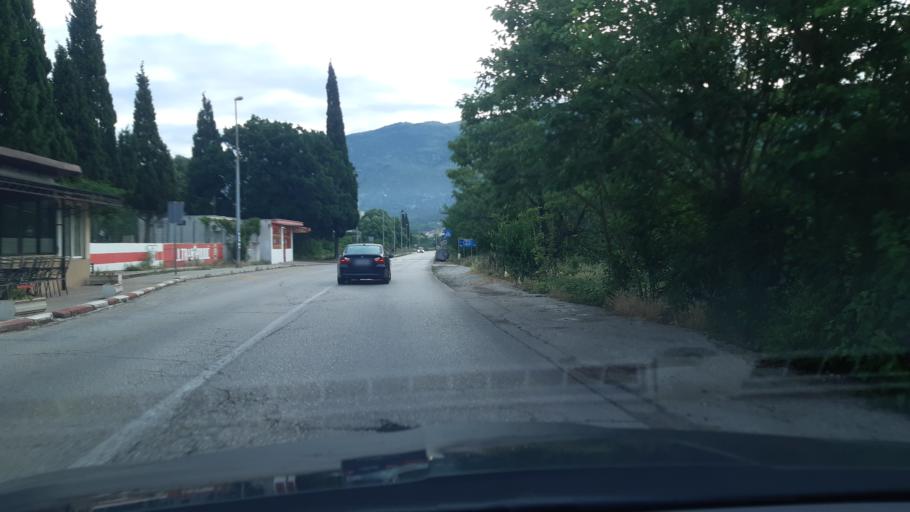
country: BA
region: Federation of Bosnia and Herzegovina
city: Rodoc
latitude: 43.3165
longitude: 17.8174
